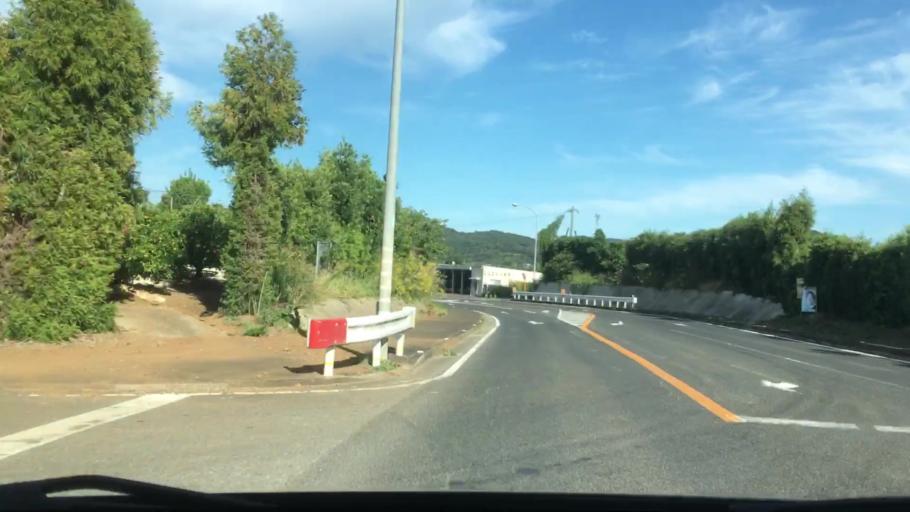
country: JP
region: Nagasaki
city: Sasebo
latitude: 33.0752
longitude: 129.7598
